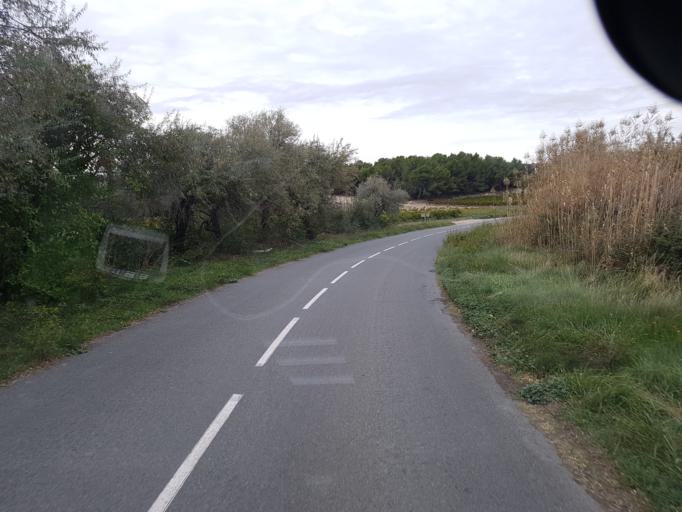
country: FR
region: Languedoc-Roussillon
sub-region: Departement de l'Aude
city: Narbonne
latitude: 43.1388
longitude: 2.9798
